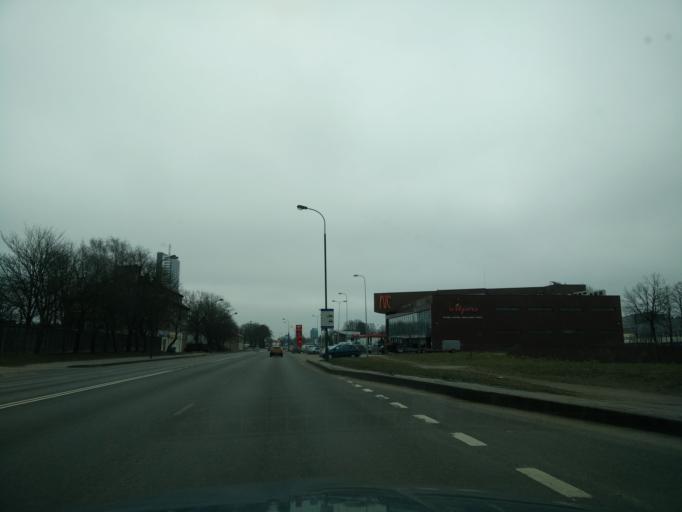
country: LT
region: Klaipedos apskritis
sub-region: Klaipeda
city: Klaipeda
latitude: 55.6957
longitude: 21.1390
